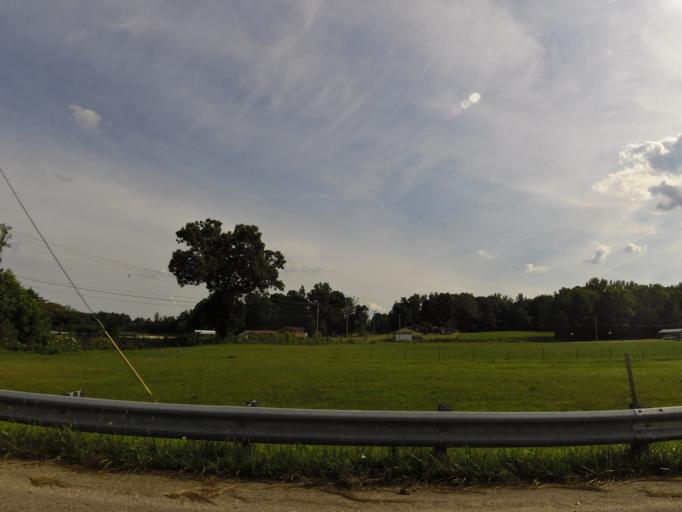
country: US
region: Tennessee
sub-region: Benton County
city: Camden
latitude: 36.0361
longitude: -88.1197
